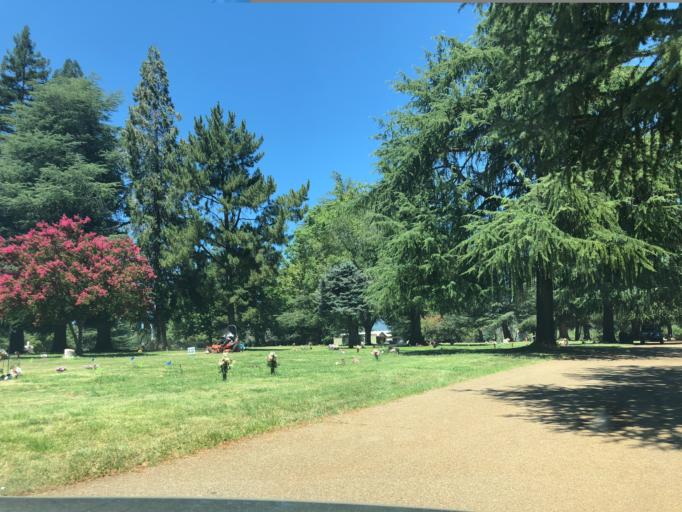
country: US
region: California
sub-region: Shasta County
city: Redding
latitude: 40.5894
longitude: -122.3855
